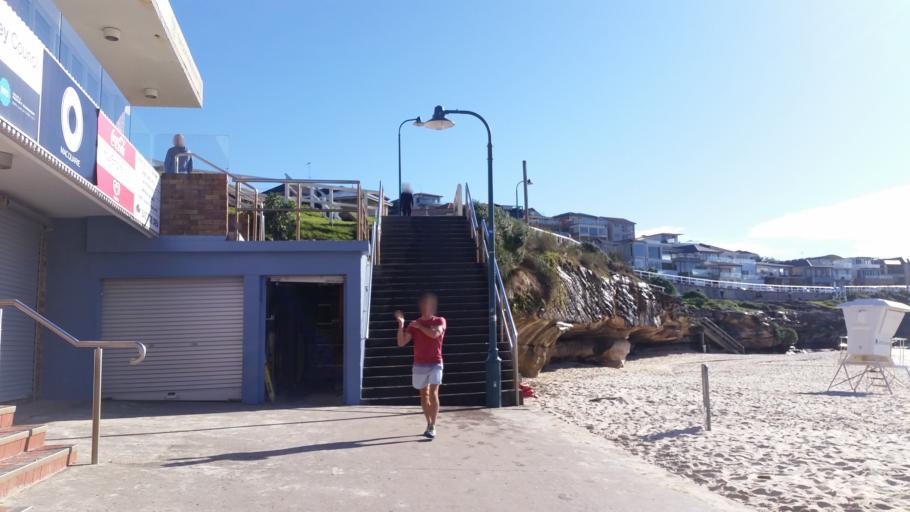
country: AU
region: New South Wales
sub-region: Waverley
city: Bronte
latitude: -33.9034
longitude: 151.2679
